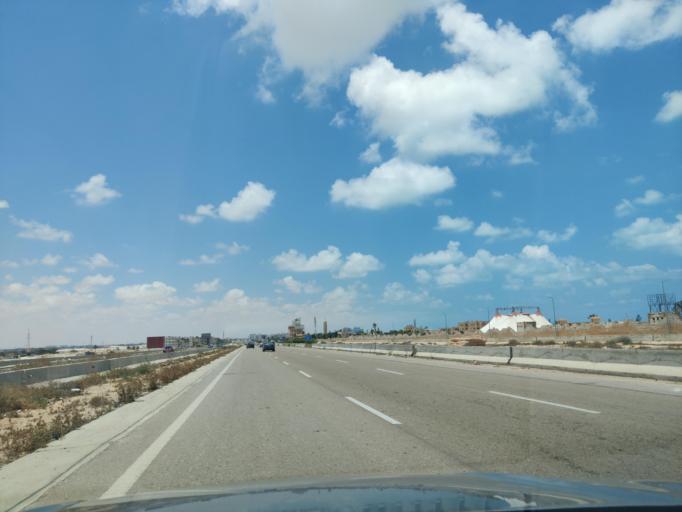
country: EG
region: Muhafazat Matruh
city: Al `Alamayn
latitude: 30.8151
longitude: 29.0386
